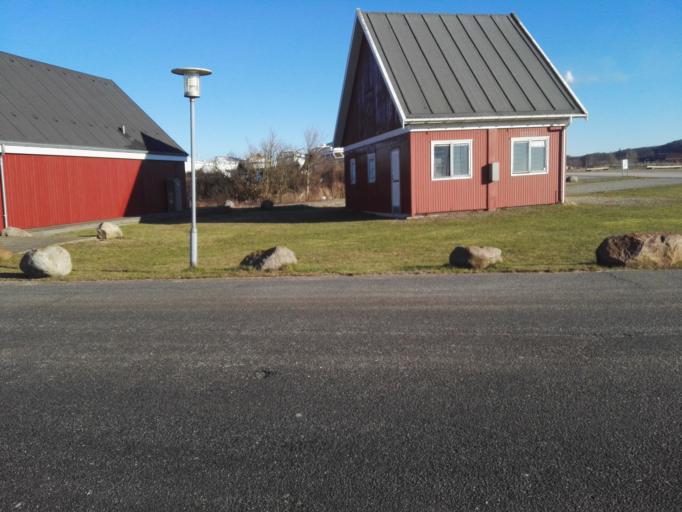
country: DK
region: Capital Region
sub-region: Halsnaes Kommune
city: Frederiksvaerk
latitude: 55.9657
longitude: 12.0005
